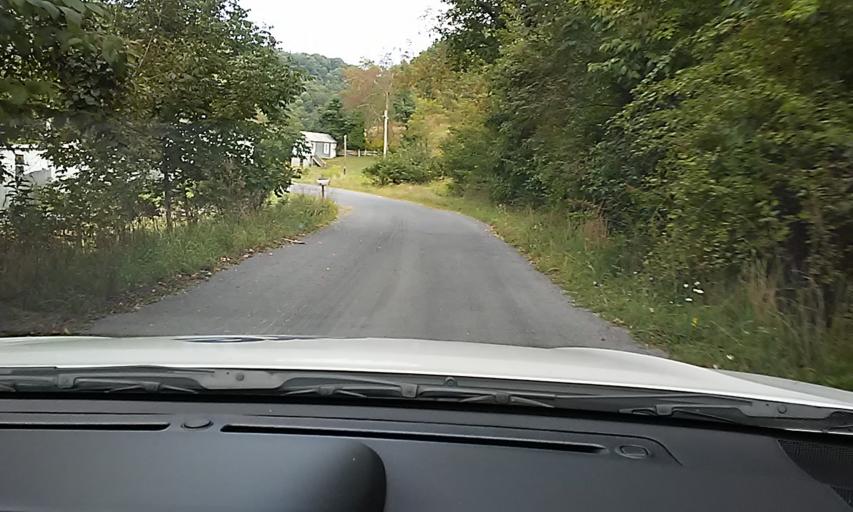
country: US
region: West Virginia
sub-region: Marion County
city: Mannington
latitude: 39.6214
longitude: -80.3508
